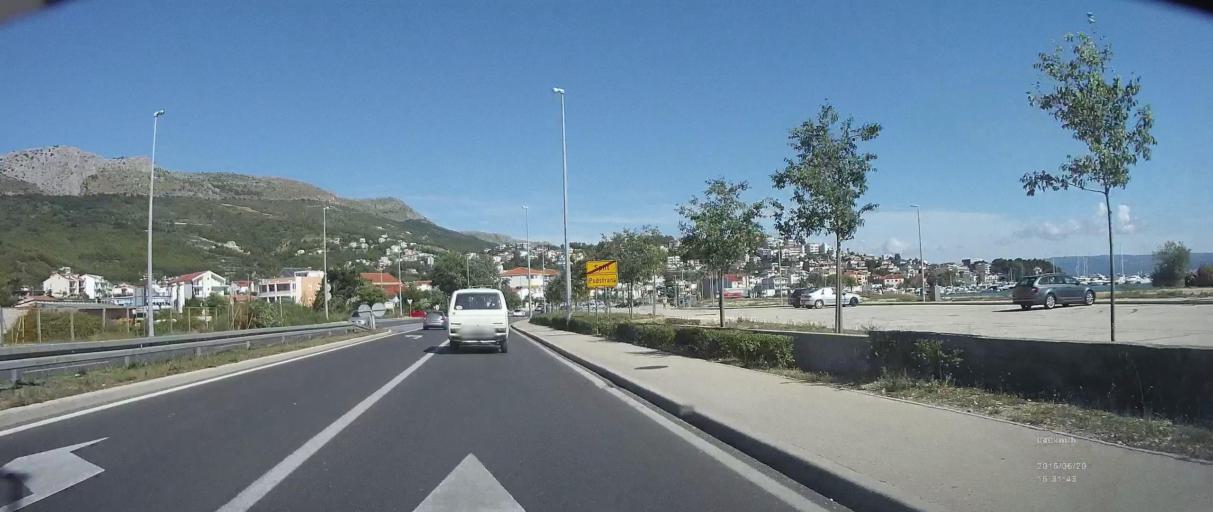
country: HR
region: Splitsko-Dalmatinska
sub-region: Grad Split
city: Stobrec
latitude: 43.5045
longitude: 16.5318
